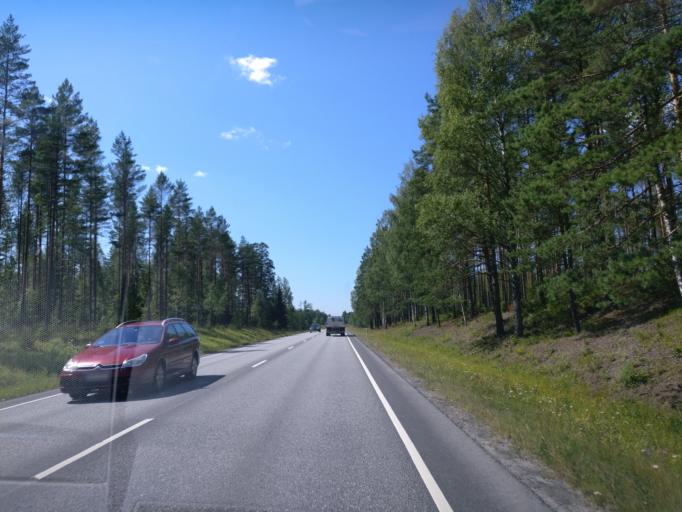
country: FI
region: Satakunta
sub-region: Pori
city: Kullaa
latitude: 61.4602
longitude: 22.0961
